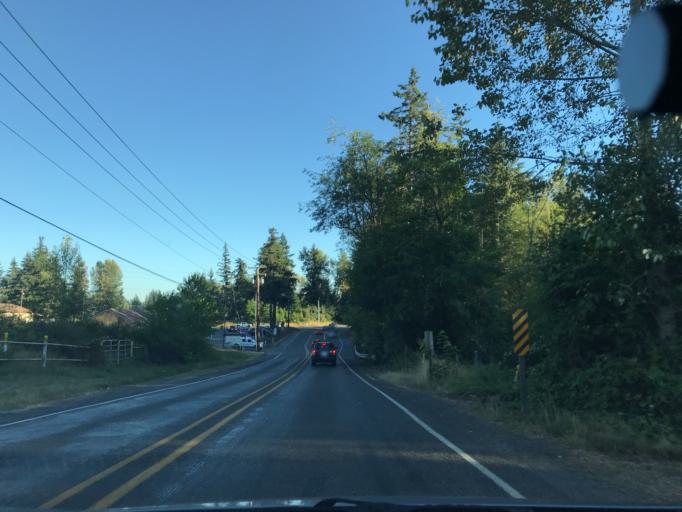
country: US
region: Washington
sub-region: King County
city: Pacific
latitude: 47.2526
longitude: -122.1870
